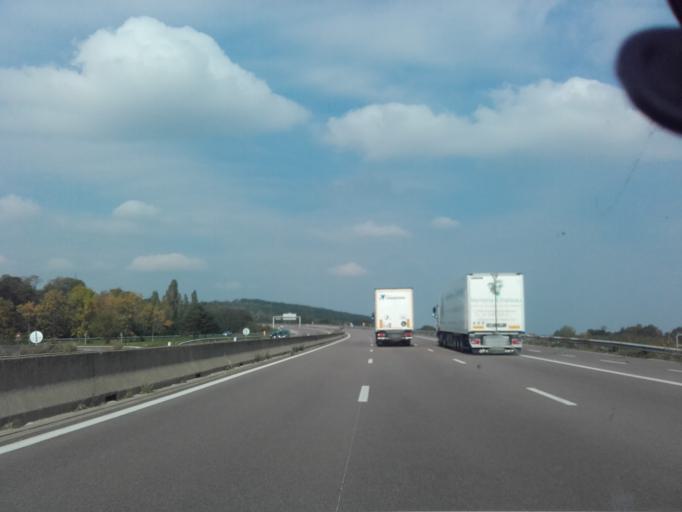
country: FR
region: Bourgogne
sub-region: Departement de Saone-et-Loire
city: Tournus
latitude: 46.5807
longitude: 4.8998
